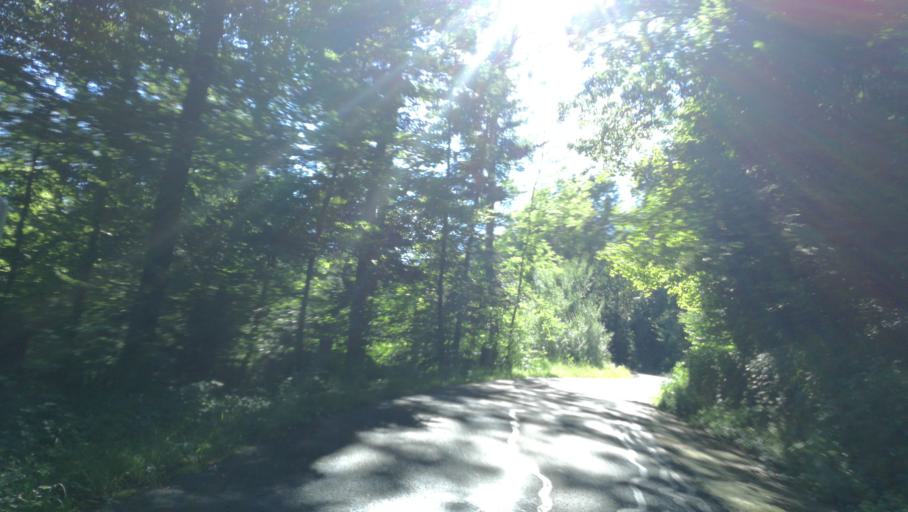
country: CH
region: Zug
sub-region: Zug
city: Unterageri
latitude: 47.1519
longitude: 8.5575
